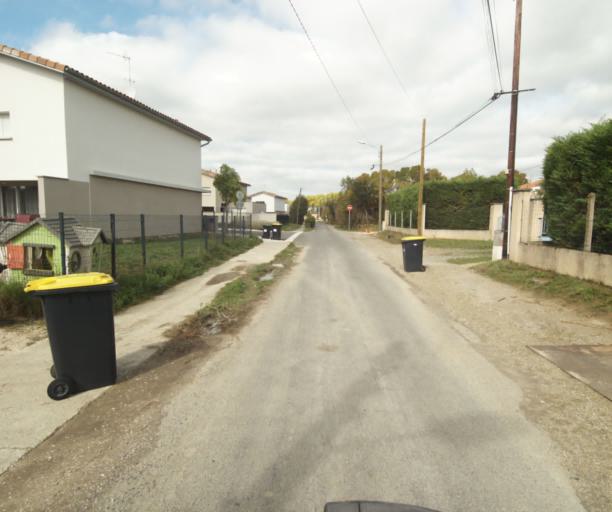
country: FR
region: Midi-Pyrenees
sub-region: Departement du Tarn-et-Garonne
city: Montech
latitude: 43.9524
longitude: 1.2245
